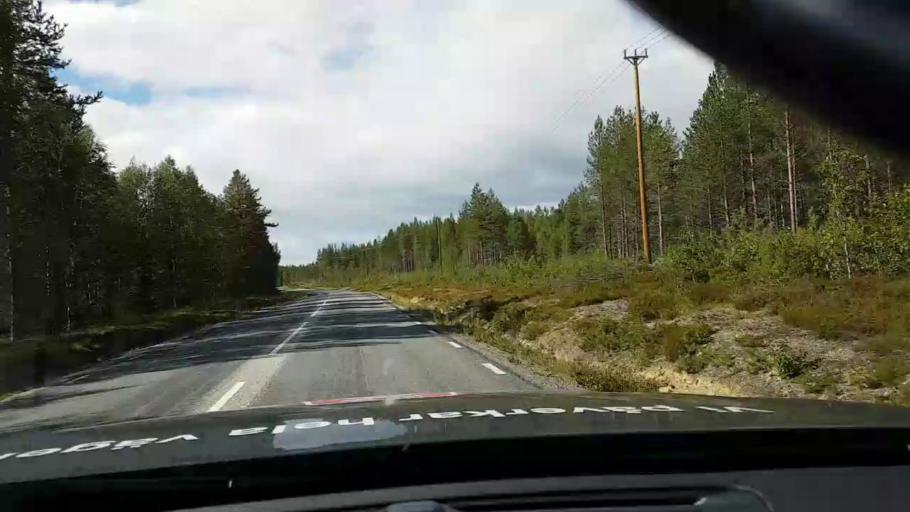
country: SE
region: Vaesterbotten
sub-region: Asele Kommun
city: Asele
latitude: 63.8473
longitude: 17.4118
